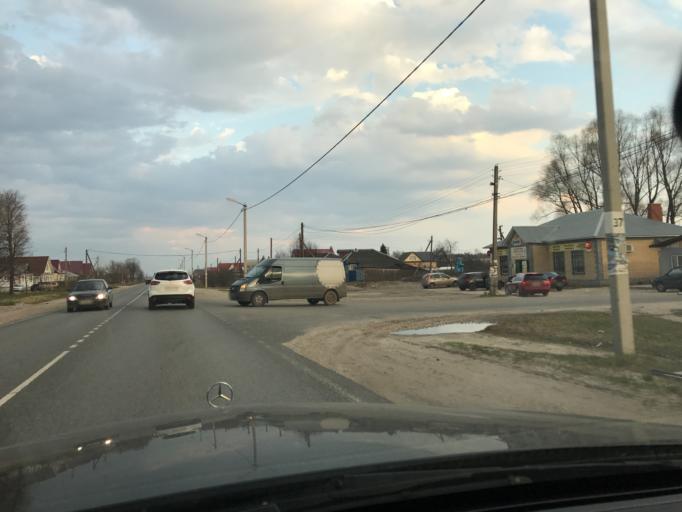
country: RU
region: Vladimir
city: Murom
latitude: 55.6089
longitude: 41.9546
